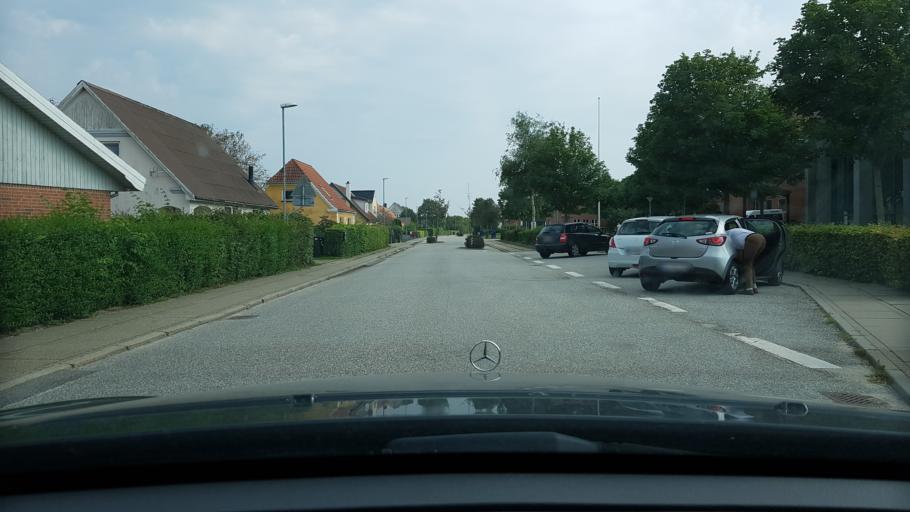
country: DK
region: North Denmark
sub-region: Alborg Kommune
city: Hals
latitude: 56.9648
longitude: 10.2231
